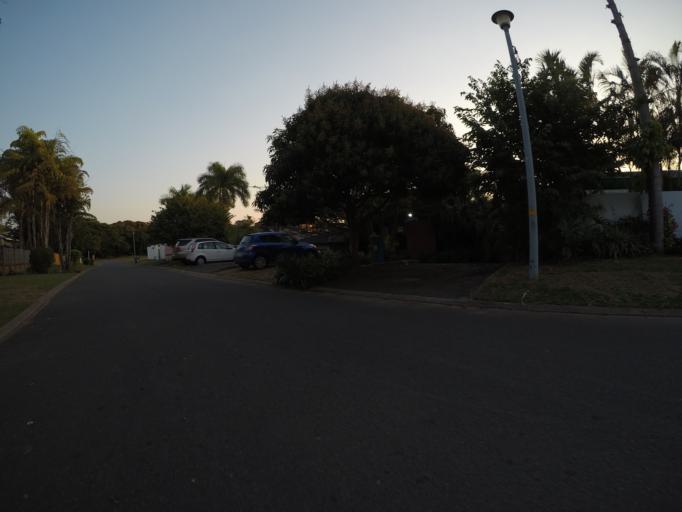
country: ZA
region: KwaZulu-Natal
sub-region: uThungulu District Municipality
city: Richards Bay
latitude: -28.7663
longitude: 32.1202
